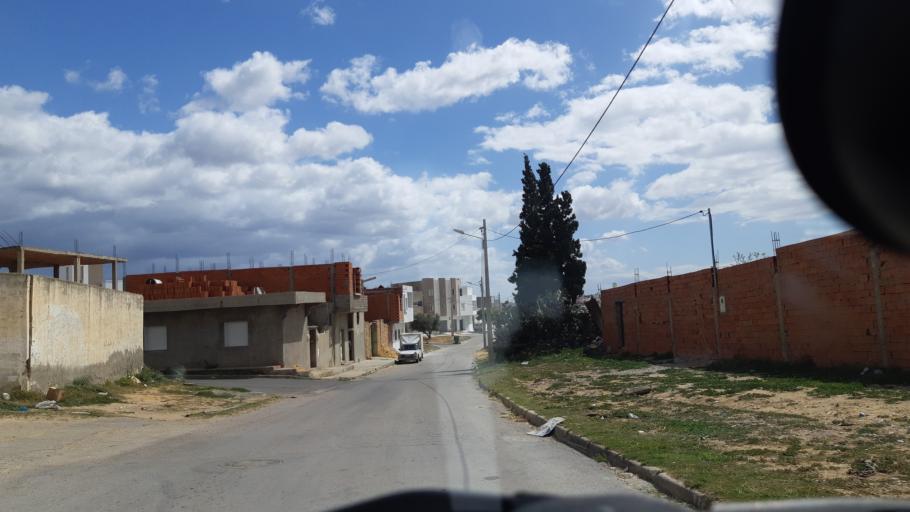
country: TN
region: Susah
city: Akouda
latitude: 35.8782
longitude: 10.5150
